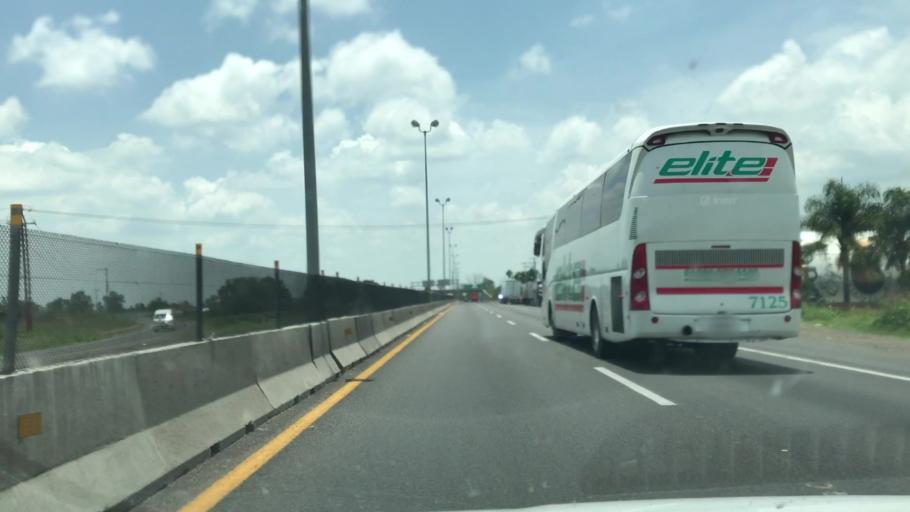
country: MX
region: Guanajuato
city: Abasolo
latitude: 20.4651
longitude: -101.5138
